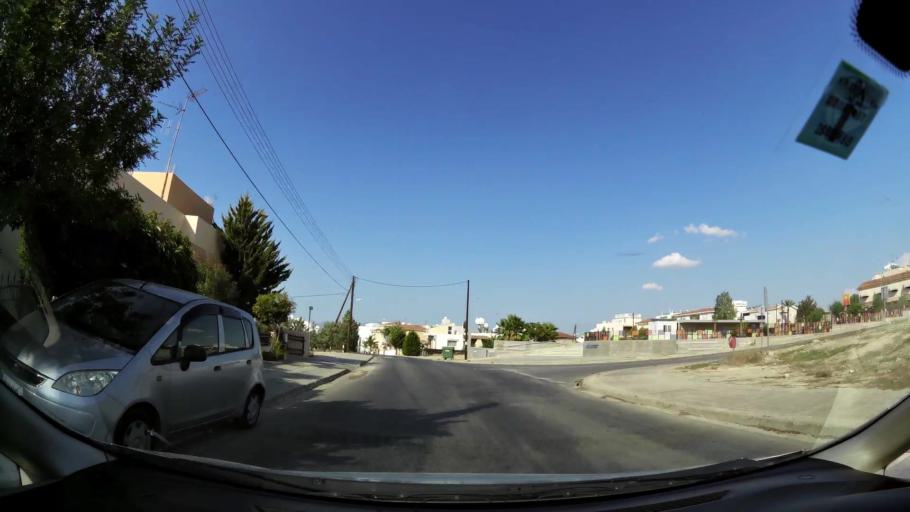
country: CY
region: Lefkosia
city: Nicosia
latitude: 35.1488
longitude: 33.3009
